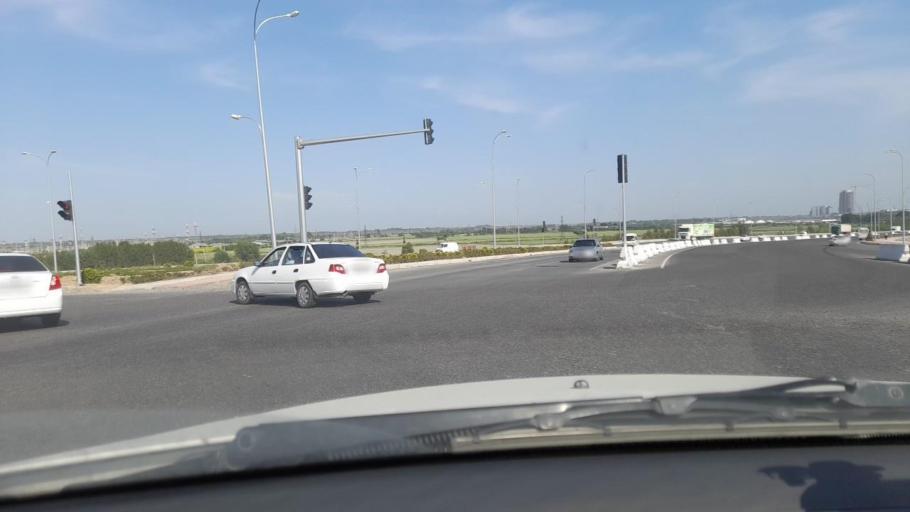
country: UZ
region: Samarqand
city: Jomboy
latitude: 39.6750
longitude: 67.0445
